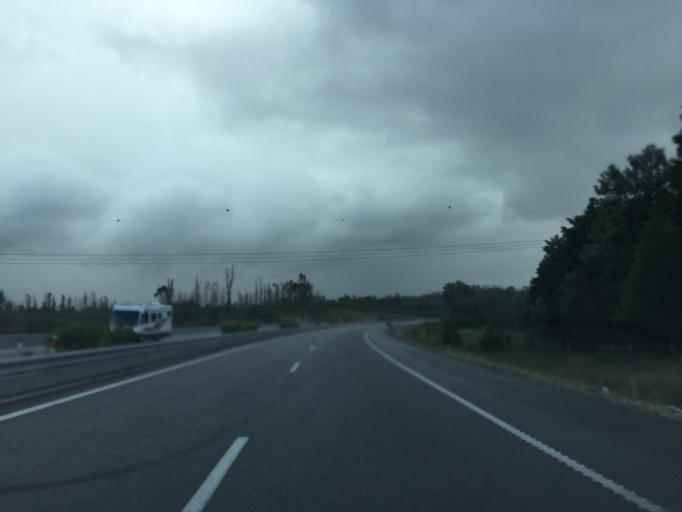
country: PT
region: Coimbra
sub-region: Cantanhede
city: Cantanhede
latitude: 40.2855
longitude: -8.5194
